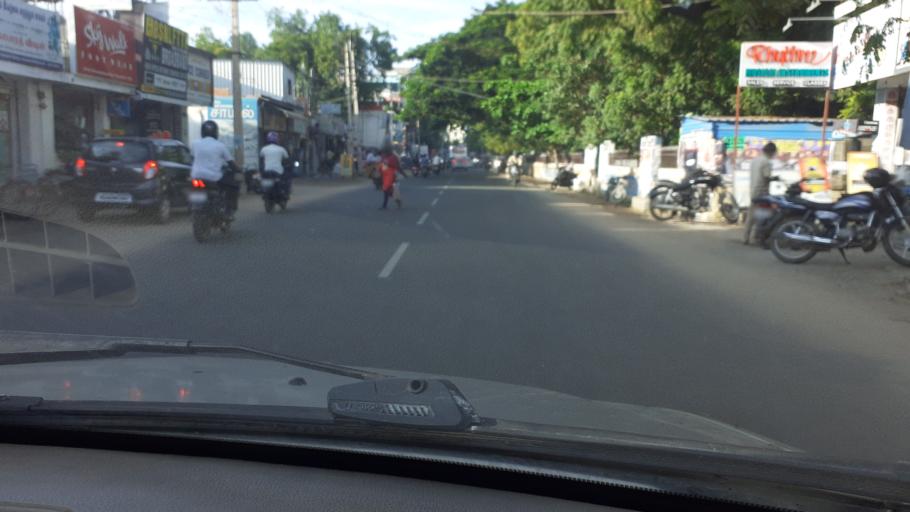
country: IN
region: Tamil Nadu
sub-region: Tirunelveli Kattabo
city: Tirunelveli
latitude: 8.7225
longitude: 77.7320
